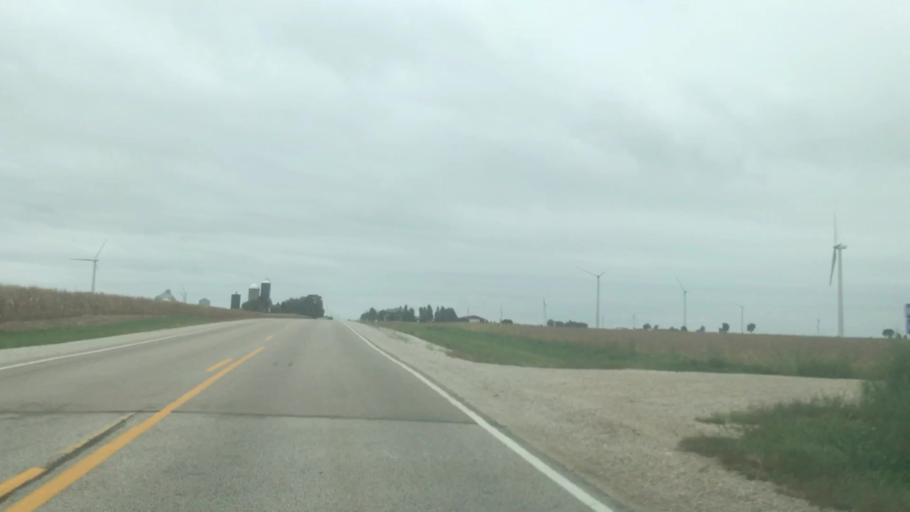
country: US
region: Wisconsin
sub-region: Fond du Lac County
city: Oakfield
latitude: 43.6321
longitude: -88.5418
